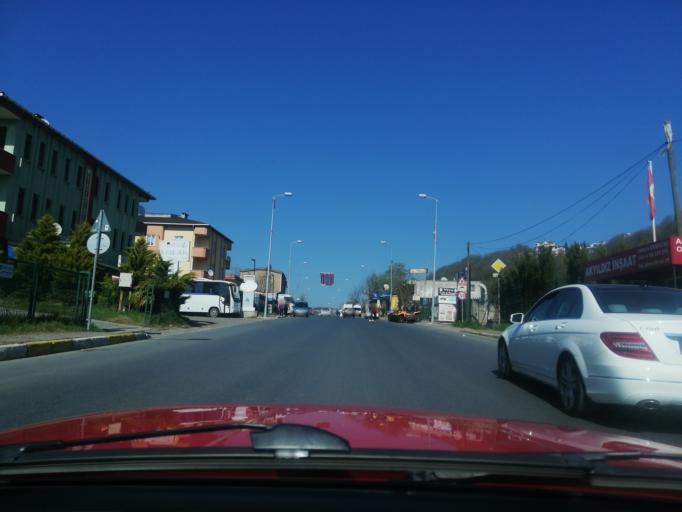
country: TR
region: Istanbul
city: Umraniye
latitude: 41.0868
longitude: 29.1367
